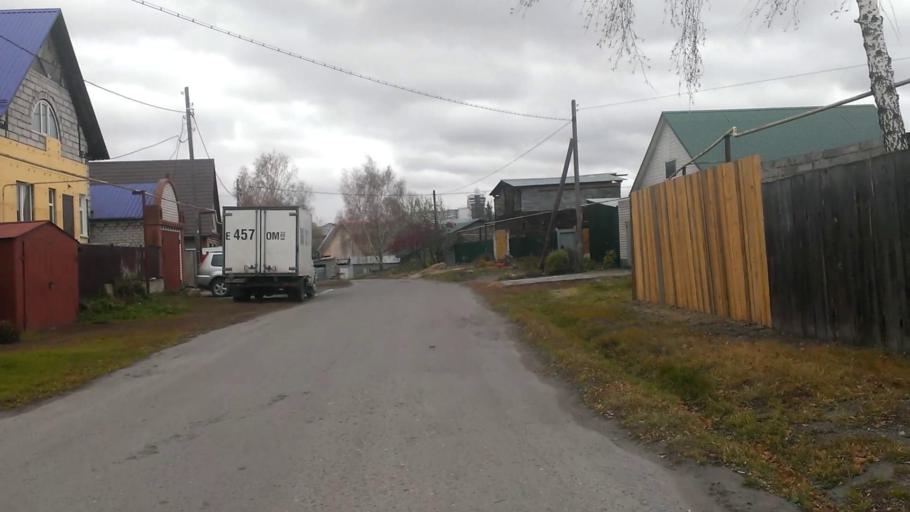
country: RU
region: Altai Krai
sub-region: Gorod Barnaulskiy
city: Barnaul
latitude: 53.3515
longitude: 83.7475
